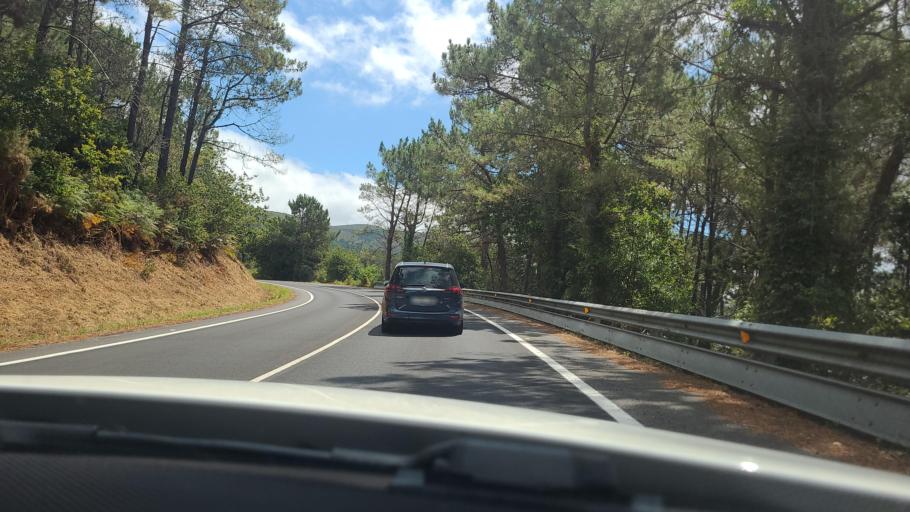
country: ES
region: Galicia
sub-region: Provincia da Coruna
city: Corcubion
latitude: 42.9388
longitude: -9.1724
